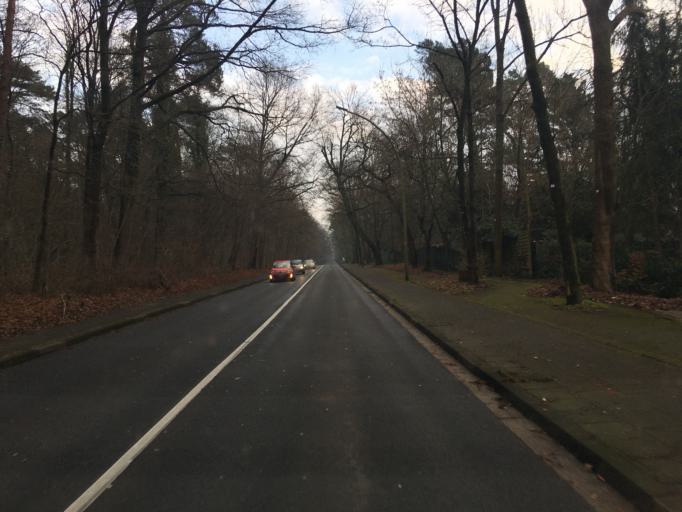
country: DE
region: North Rhine-Westphalia
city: Opladen
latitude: 51.0234
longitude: 7.0588
